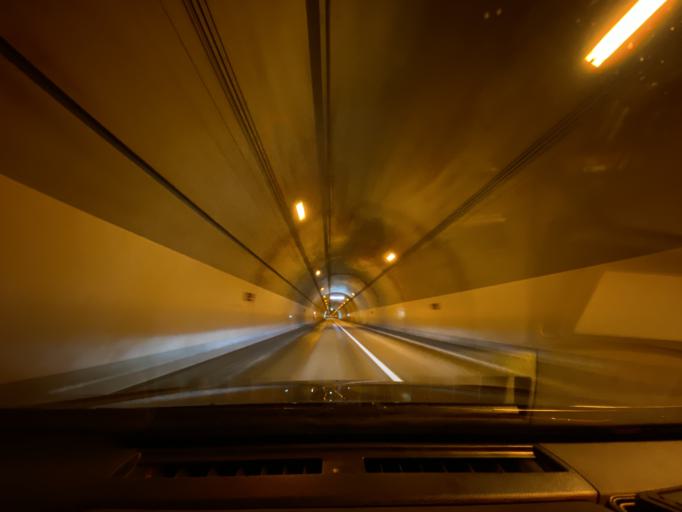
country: JP
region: Hokkaido
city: Rumoi
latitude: 43.8103
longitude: 141.4058
